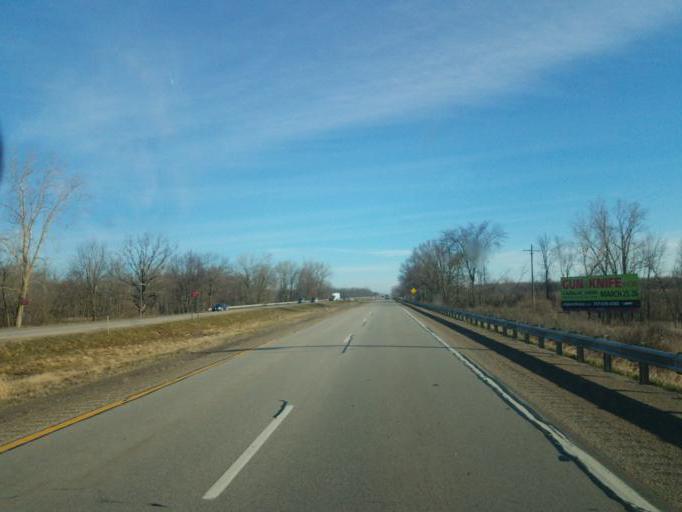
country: US
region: Michigan
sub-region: Clinton County
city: Saint Johns
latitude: 43.1364
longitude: -84.5632
